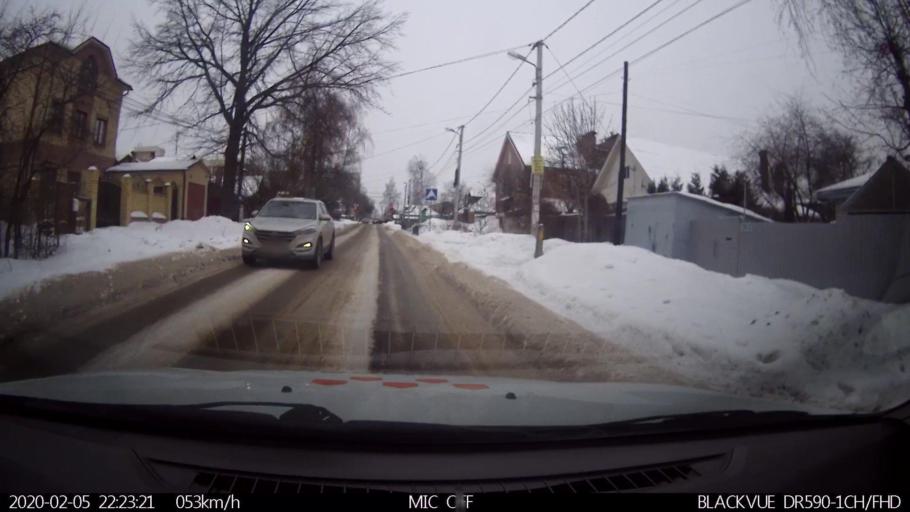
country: RU
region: Nizjnij Novgorod
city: Pervomaysk
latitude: 54.7660
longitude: 44.0272
